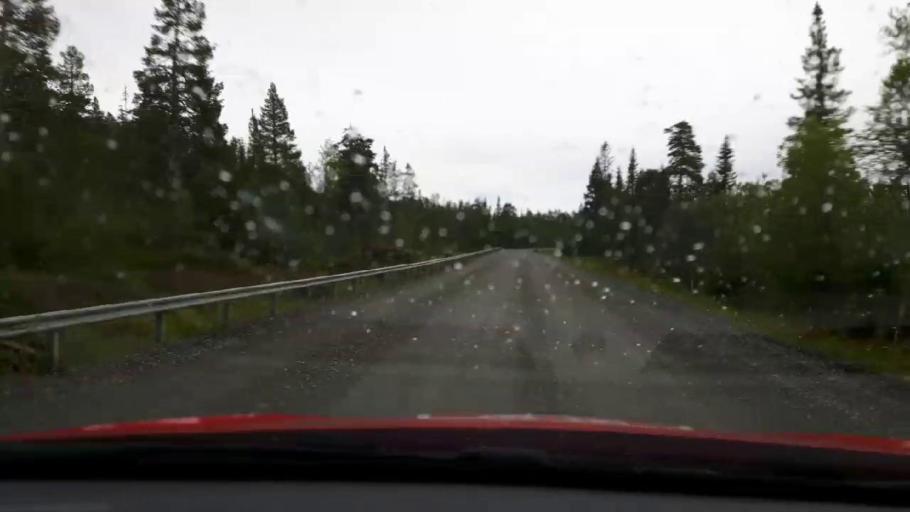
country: NO
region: Nord-Trondelag
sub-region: Meraker
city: Meraker
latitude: 63.6428
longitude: 12.2711
